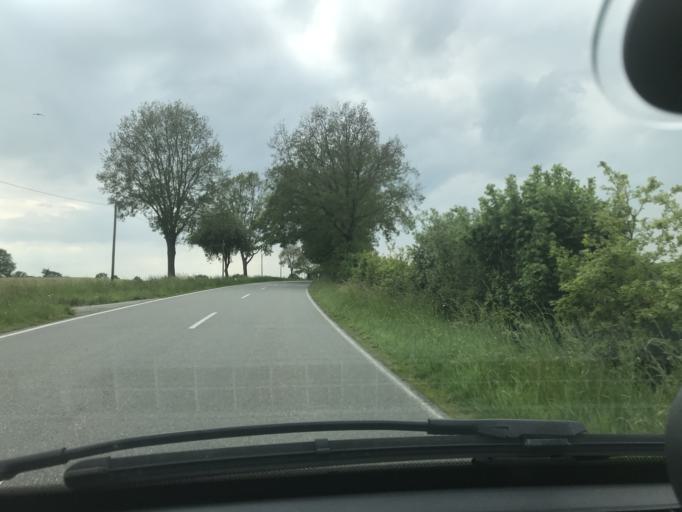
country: DE
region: Schleswig-Holstein
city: Siek
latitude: 53.6128
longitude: 10.3143
